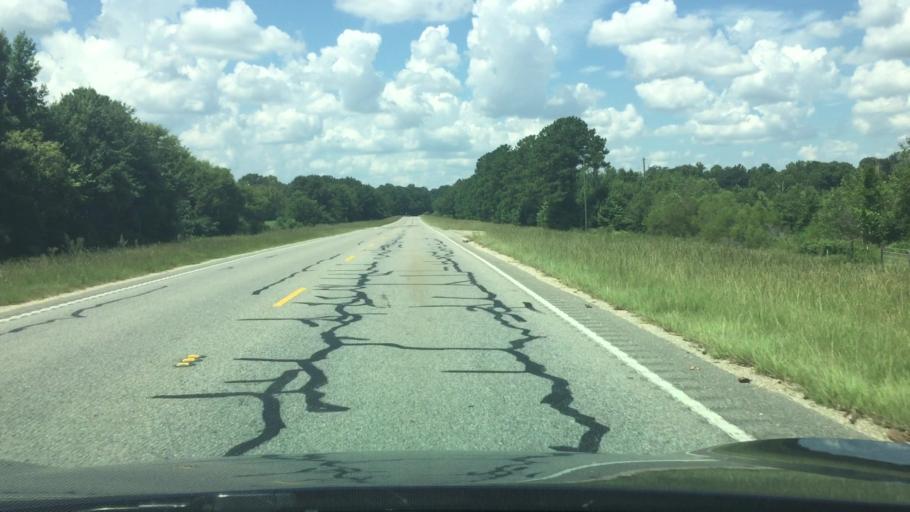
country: US
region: Alabama
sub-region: Montgomery County
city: Pike Road
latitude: 32.3722
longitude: -86.0078
